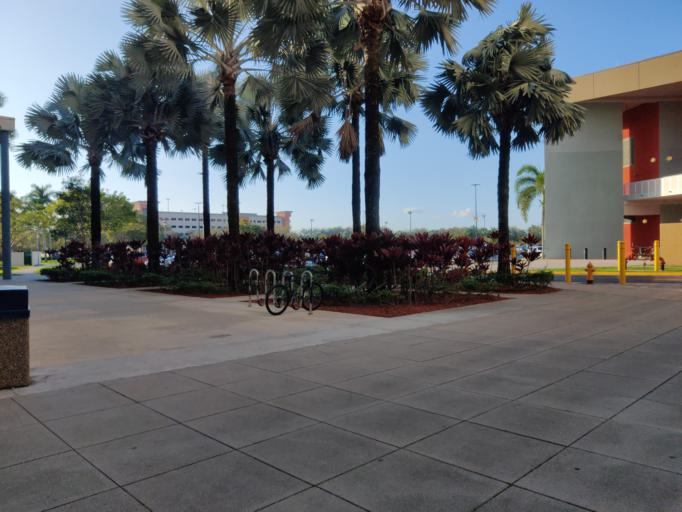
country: US
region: Florida
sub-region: Miami-Dade County
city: Sweetwater
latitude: 25.7572
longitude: -80.3773
